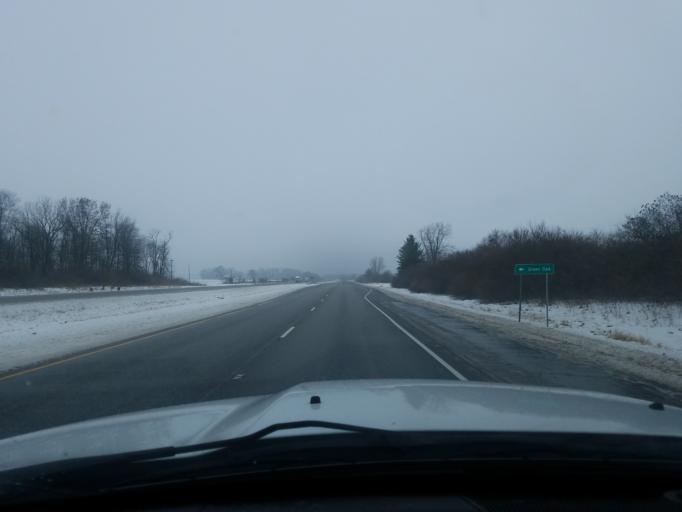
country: US
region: Indiana
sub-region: Fulton County
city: Rochester
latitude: 40.9940
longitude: -86.1677
